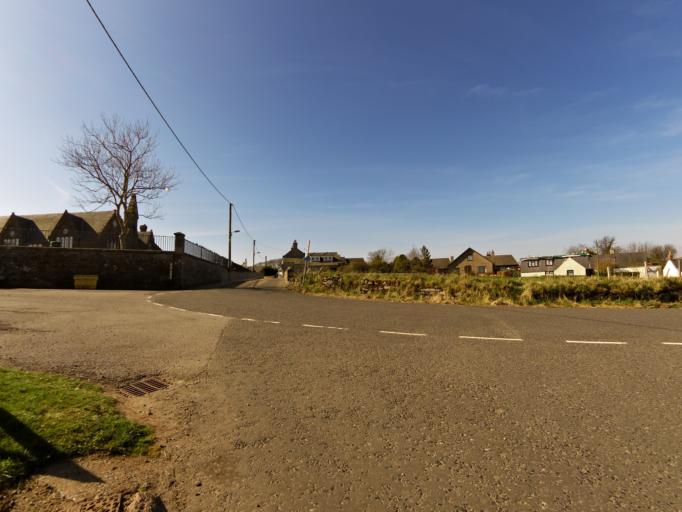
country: GB
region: Scotland
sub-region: Aberdeenshire
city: Laurencekirk
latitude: 56.7740
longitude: -2.4112
